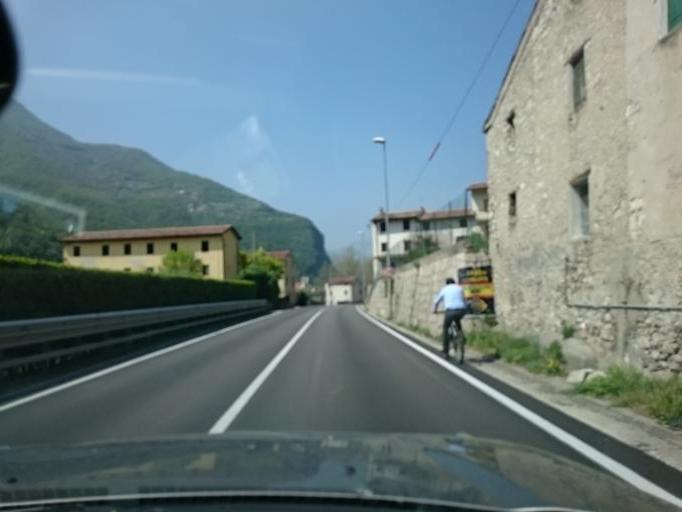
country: IT
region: Veneto
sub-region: Provincia di Vicenza
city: Campolongo sul Brenta
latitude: 45.8254
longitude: 11.7071
